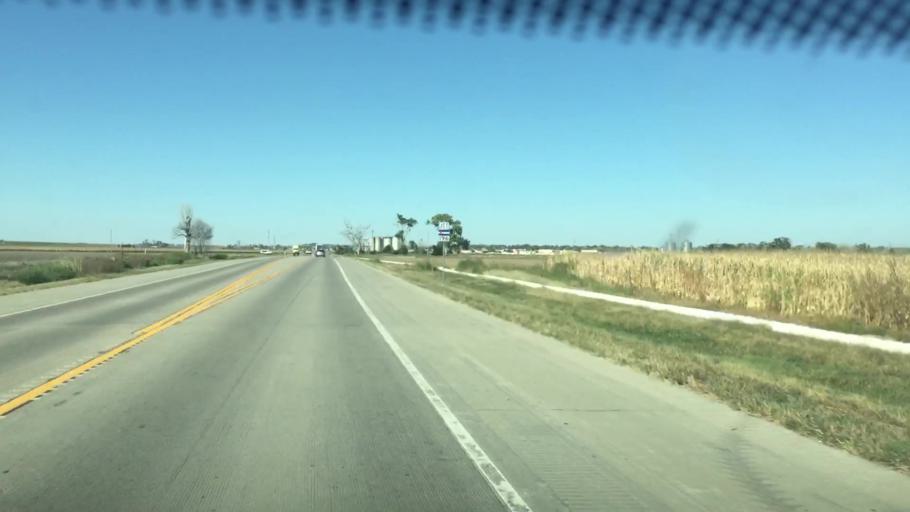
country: US
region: Colorado
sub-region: Prowers County
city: Lamar
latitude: 38.1393
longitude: -102.7237
